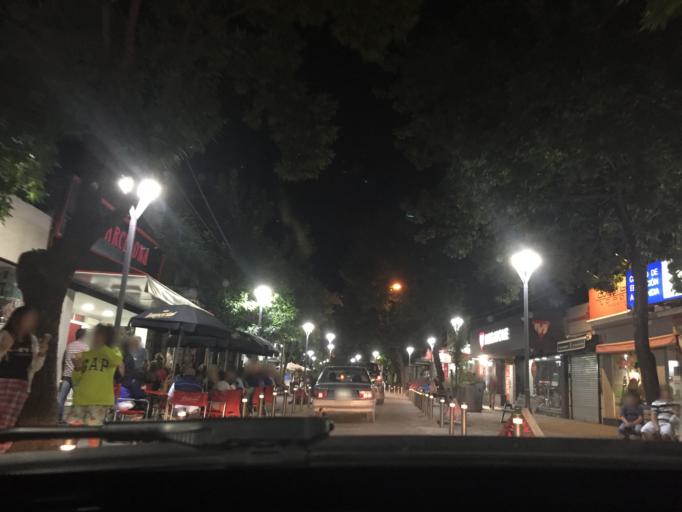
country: AR
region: Cordoba
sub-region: Departamento de Calamuchita
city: Santa Rosa de Calamuchita
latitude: -32.0689
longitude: -64.5372
